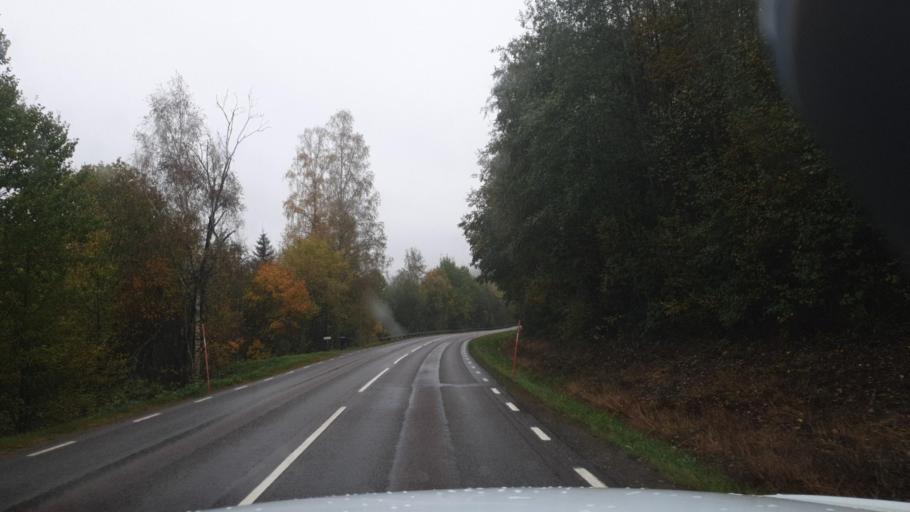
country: SE
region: Vaermland
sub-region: Eda Kommun
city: Amotfors
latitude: 59.6955
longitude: 12.3412
